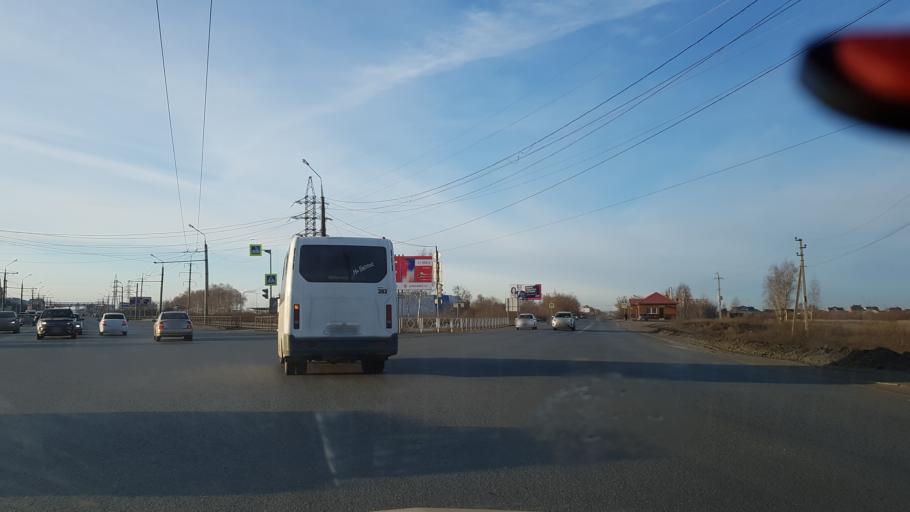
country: RU
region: Samara
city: Tol'yatti
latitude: 53.5451
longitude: 49.3806
